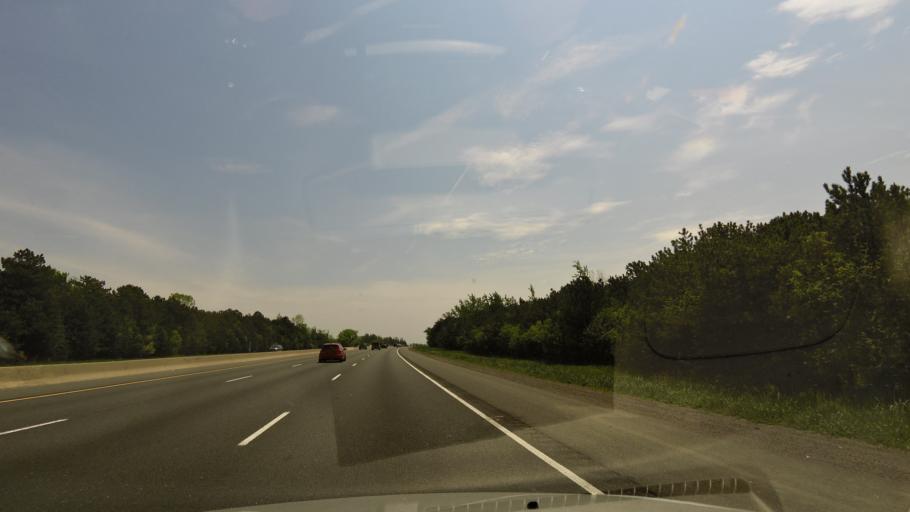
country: CA
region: Ontario
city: Oshawa
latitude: 43.8833
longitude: -78.8104
